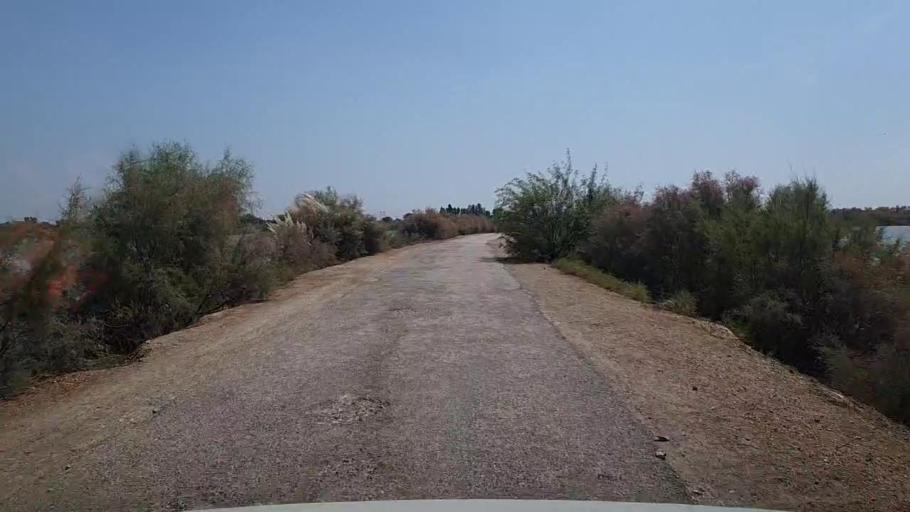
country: PK
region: Sindh
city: Kandhkot
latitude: 28.2964
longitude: 69.3520
